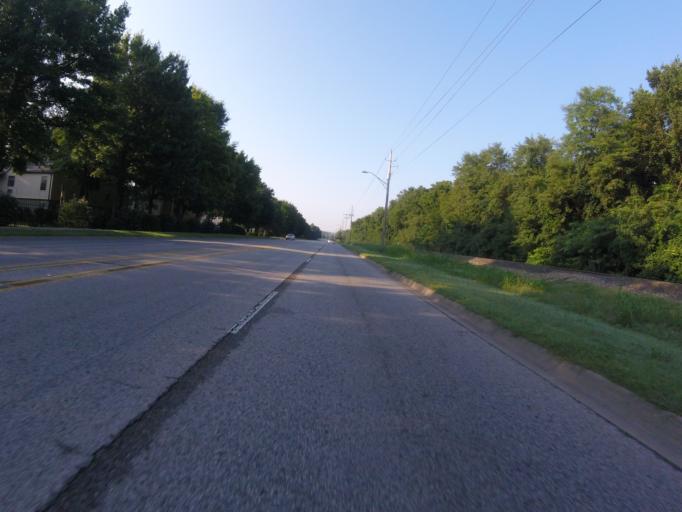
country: US
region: Arkansas
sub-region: Washington County
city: Johnson
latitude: 36.1075
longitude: -94.1636
